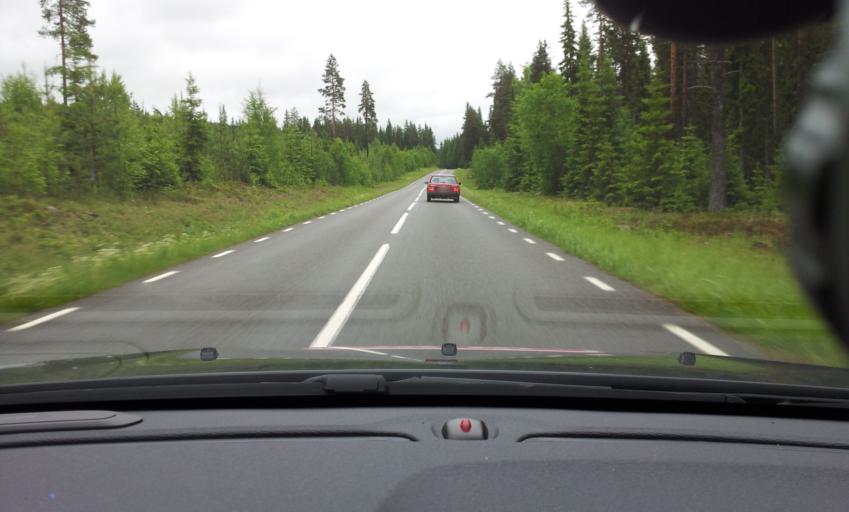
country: SE
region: Jaemtland
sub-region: Stroemsunds Kommun
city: Stroemsund
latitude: 63.4479
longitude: 15.4712
